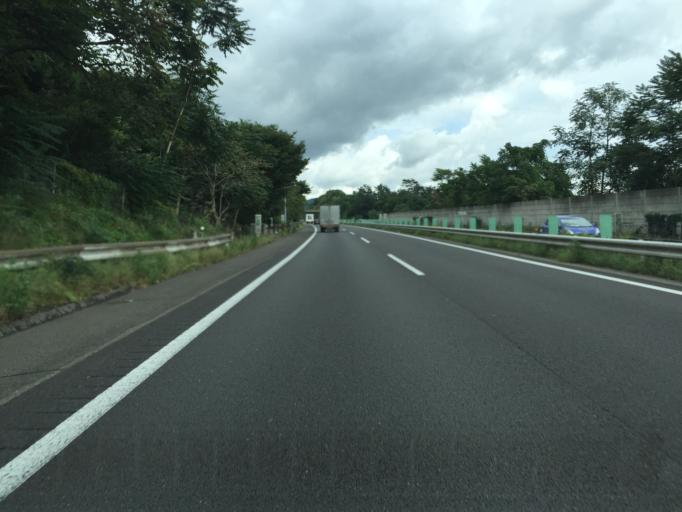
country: JP
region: Fukushima
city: Hobaramachi
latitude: 37.8548
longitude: 140.5122
